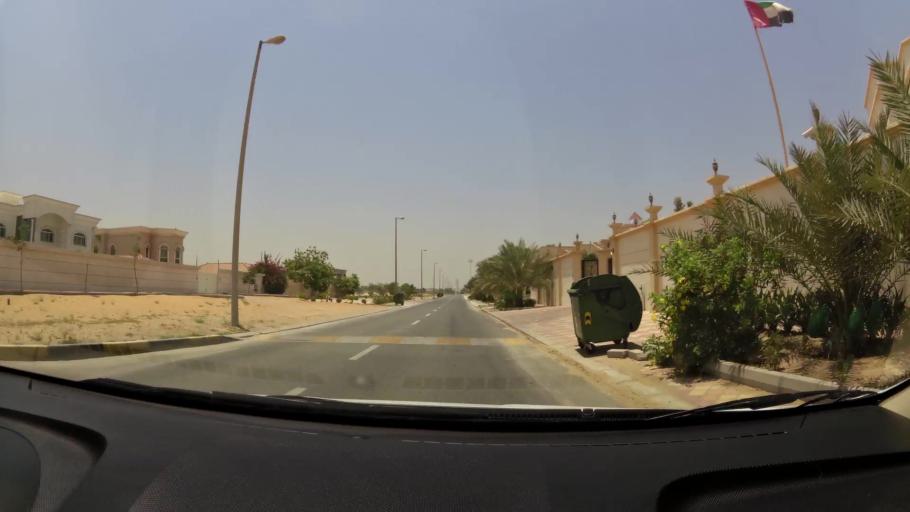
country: AE
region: Ajman
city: Ajman
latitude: 25.4096
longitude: 55.4977
